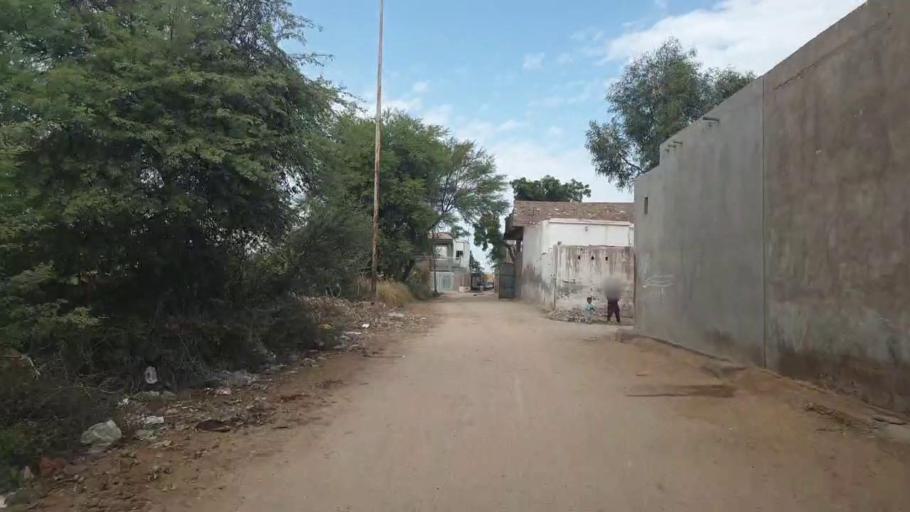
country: PK
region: Sindh
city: Sakrand
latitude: 25.9908
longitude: 68.3576
